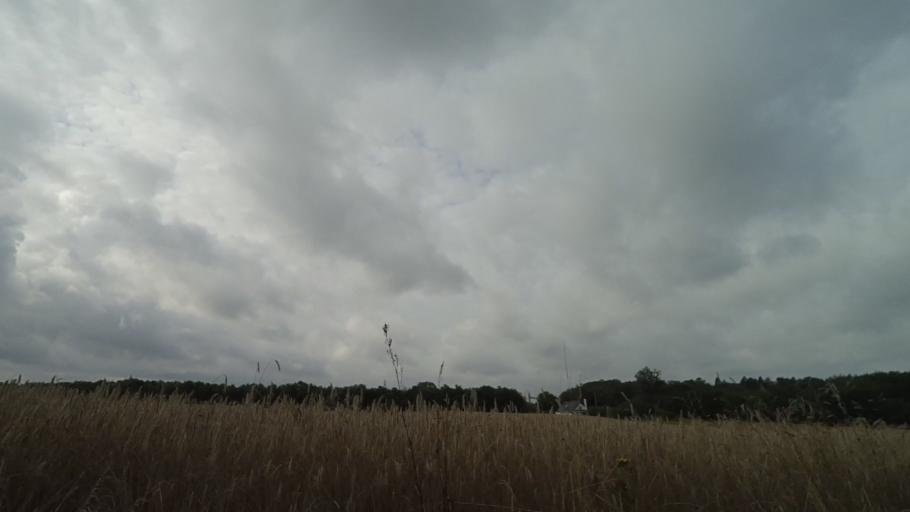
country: DK
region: Central Jutland
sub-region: Syddjurs Kommune
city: Ryomgard
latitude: 56.3999
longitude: 10.4916
